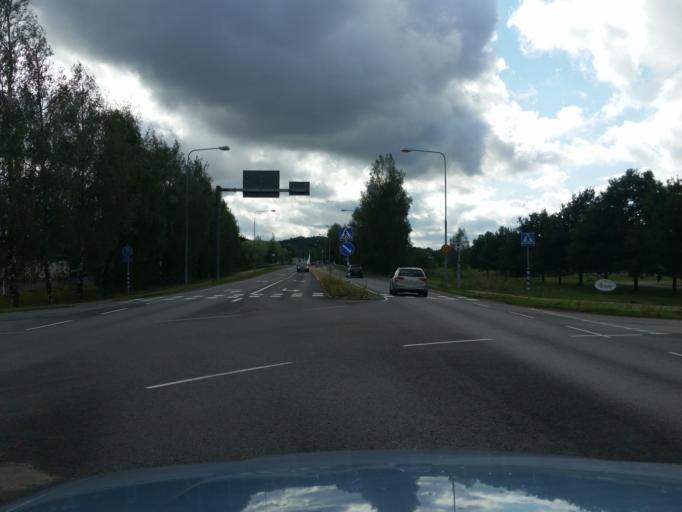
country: FI
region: Varsinais-Suomi
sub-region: Aboland-Turunmaa
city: Pargas
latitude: 60.3094
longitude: 22.3081
